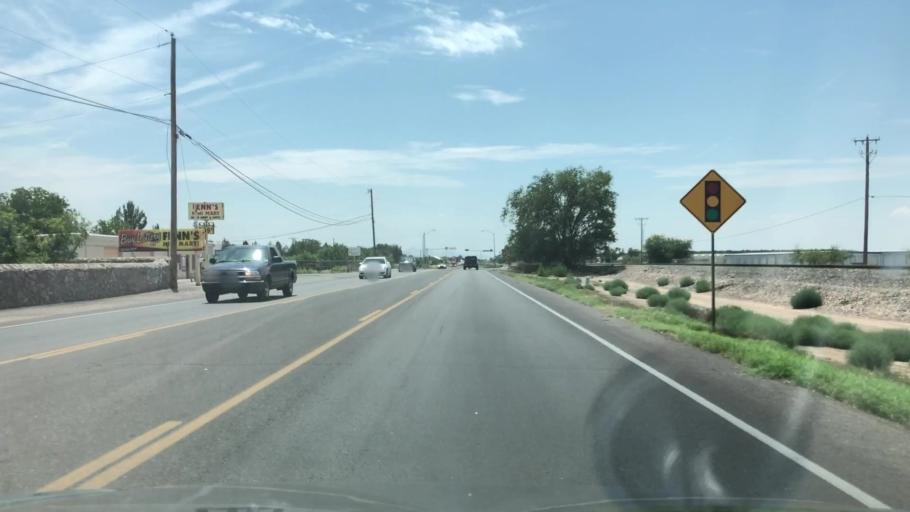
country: US
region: New Mexico
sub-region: Dona Ana County
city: University Park
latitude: 32.2635
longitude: -106.7592
